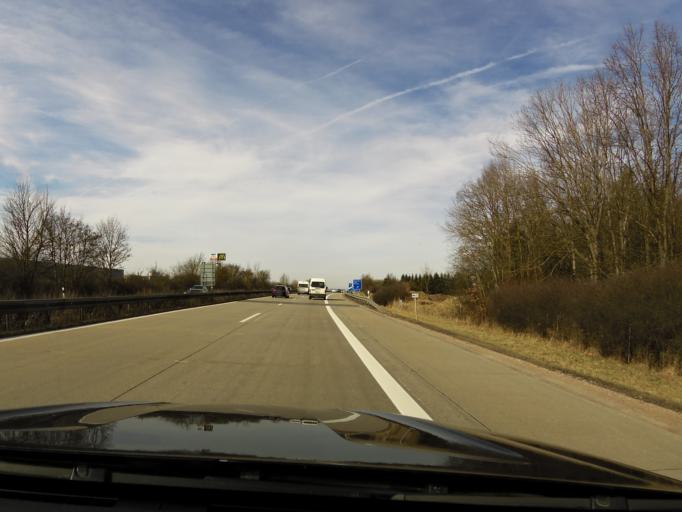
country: DE
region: Bavaria
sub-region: Upper Palatinate
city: Pentling
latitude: 48.9727
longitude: 12.0678
